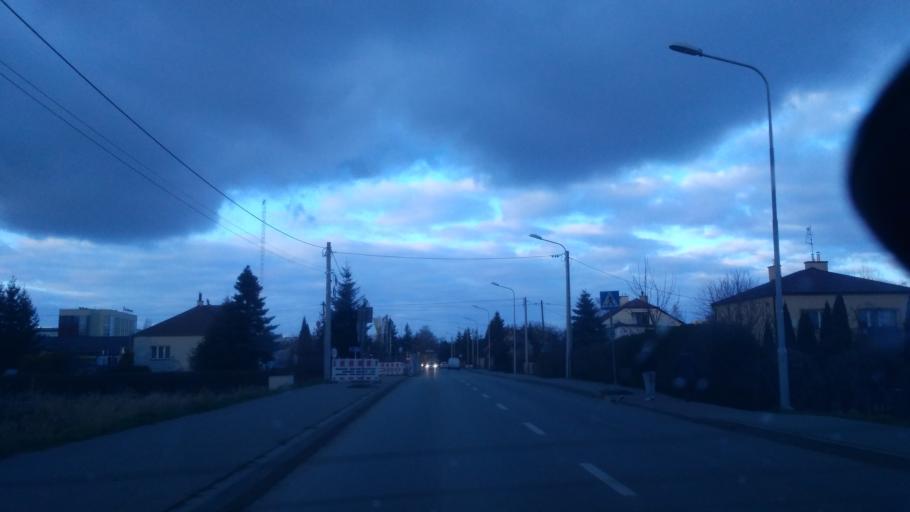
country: PL
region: Subcarpathian Voivodeship
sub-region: Rzeszow
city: Rzeszow
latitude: 50.0275
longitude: 22.0423
